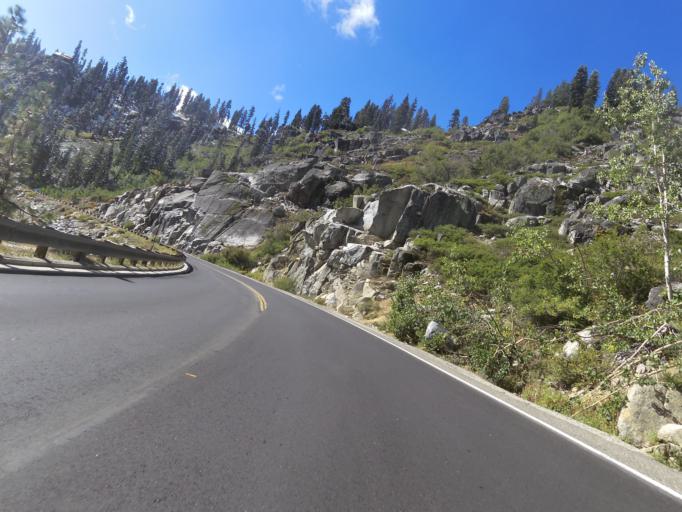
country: US
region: California
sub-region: El Dorado County
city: South Lake Tahoe
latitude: 38.8336
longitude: -120.0355
